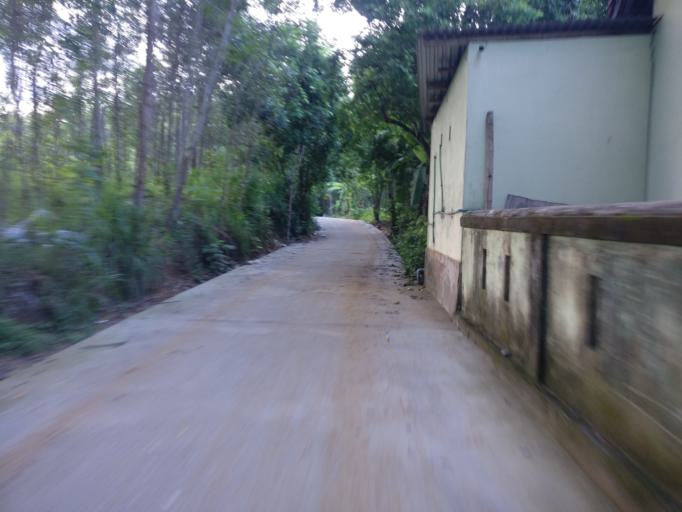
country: VN
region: Thua Thien-Hue
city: Hue
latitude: 16.3908
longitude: 107.5751
